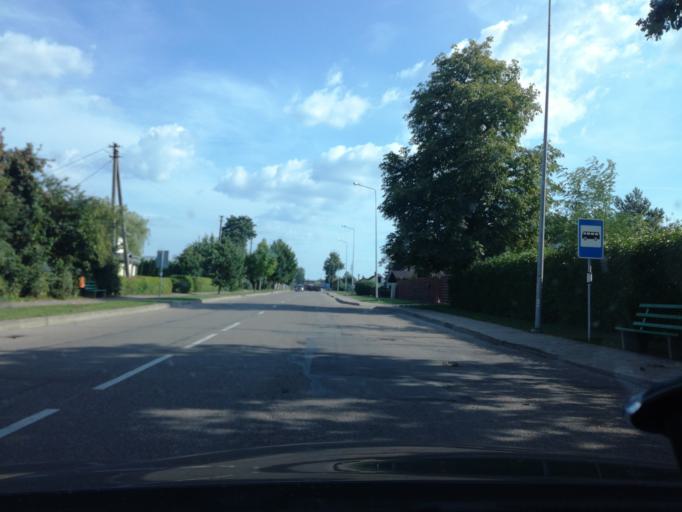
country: LT
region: Marijampoles apskritis
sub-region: Marijampole Municipality
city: Marijampole
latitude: 54.5419
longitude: 23.3493
